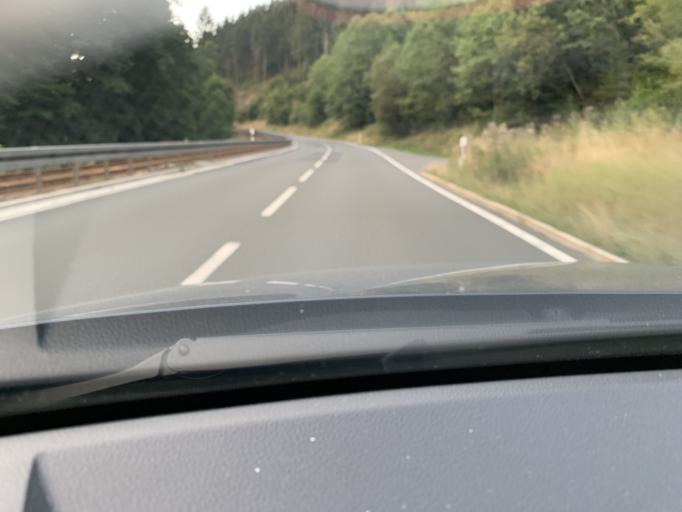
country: DE
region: Thuringia
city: Steinach
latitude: 50.4150
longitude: 11.1752
